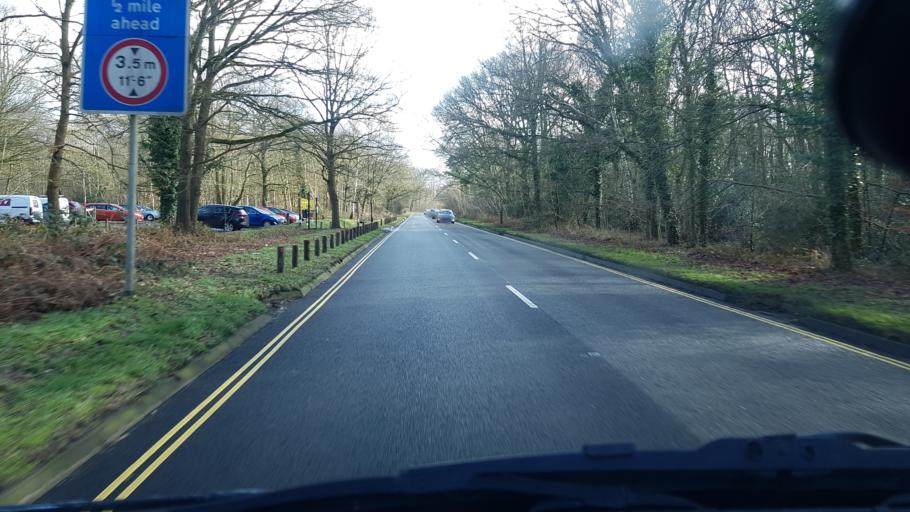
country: GB
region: England
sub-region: Surrey
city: Guildford
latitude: 51.2674
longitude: -0.5952
